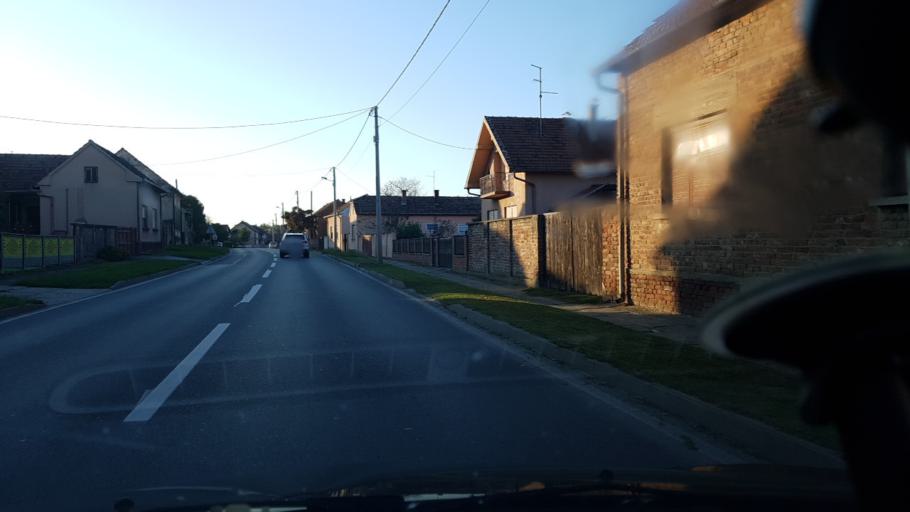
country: HR
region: Koprivnicko-Krizevacka
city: Virje
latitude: 46.0663
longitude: 16.9832
